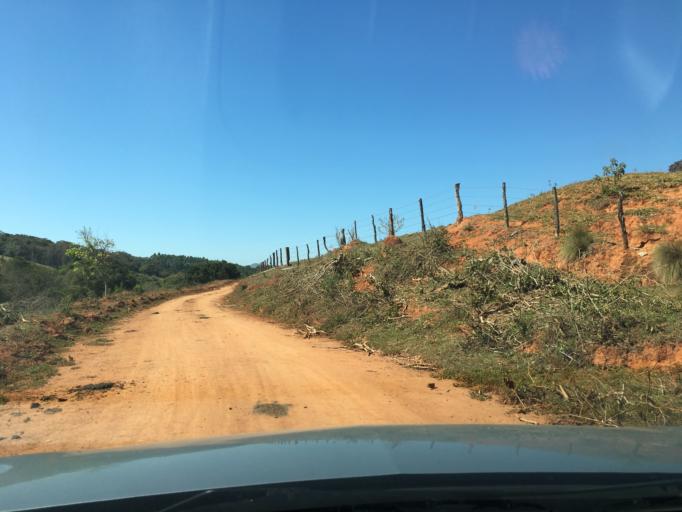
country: BR
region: Minas Gerais
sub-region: Campestre
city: Campestre
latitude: -21.5960
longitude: -46.2061
